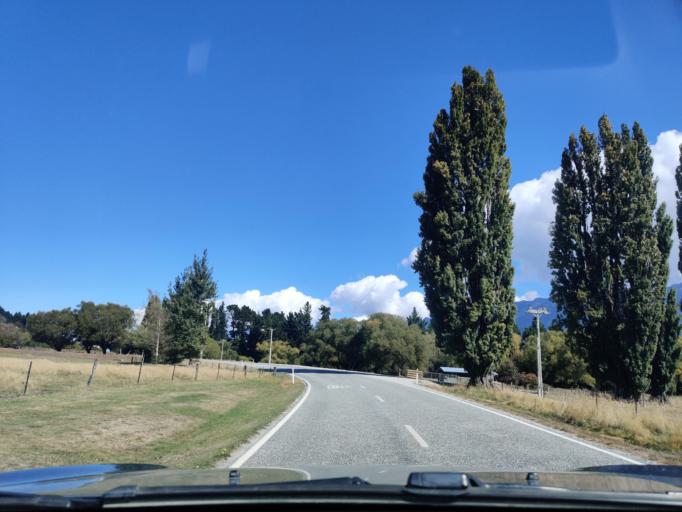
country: NZ
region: Otago
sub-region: Queenstown-Lakes District
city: Queenstown
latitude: -44.7985
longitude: 168.3989
